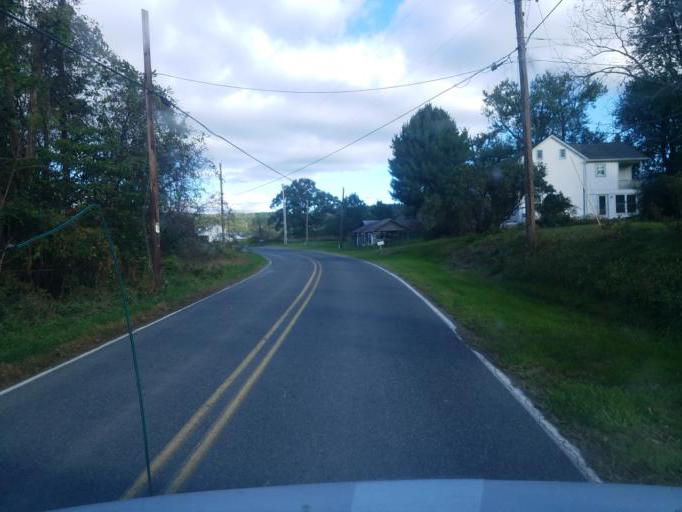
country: US
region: Pennsylvania
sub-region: Adams County
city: Biglerville
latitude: 39.8887
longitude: -77.3691
